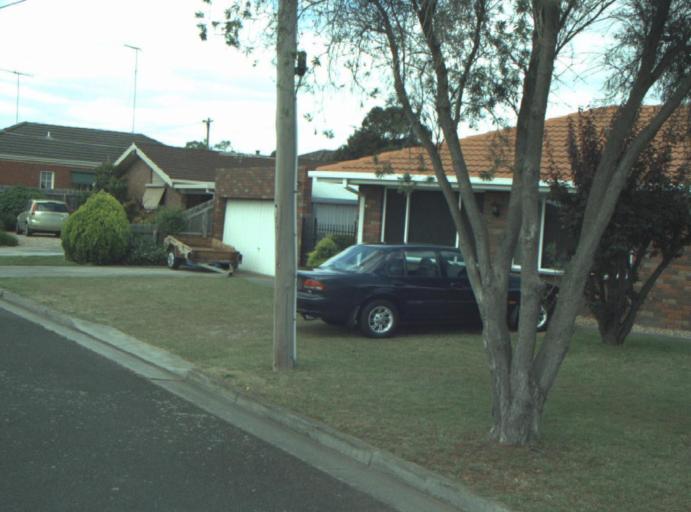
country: AU
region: Victoria
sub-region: Greater Geelong
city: Breakwater
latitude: -38.2029
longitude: 144.3378
